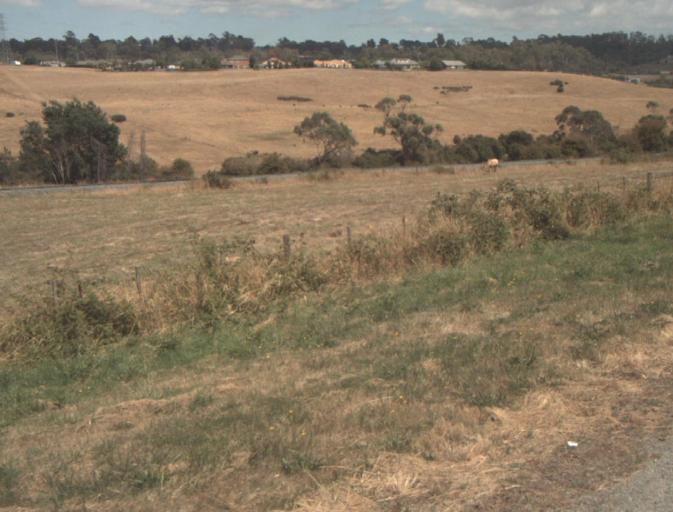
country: AU
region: Tasmania
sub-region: Launceston
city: Newstead
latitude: -41.4775
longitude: 147.1896
